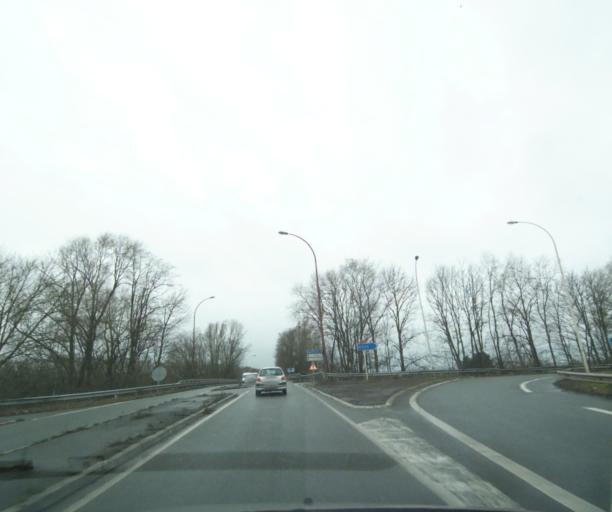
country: FR
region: Nord-Pas-de-Calais
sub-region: Departement du Nord
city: Aubry-du-Hainaut
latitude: 50.3785
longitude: 3.4711
